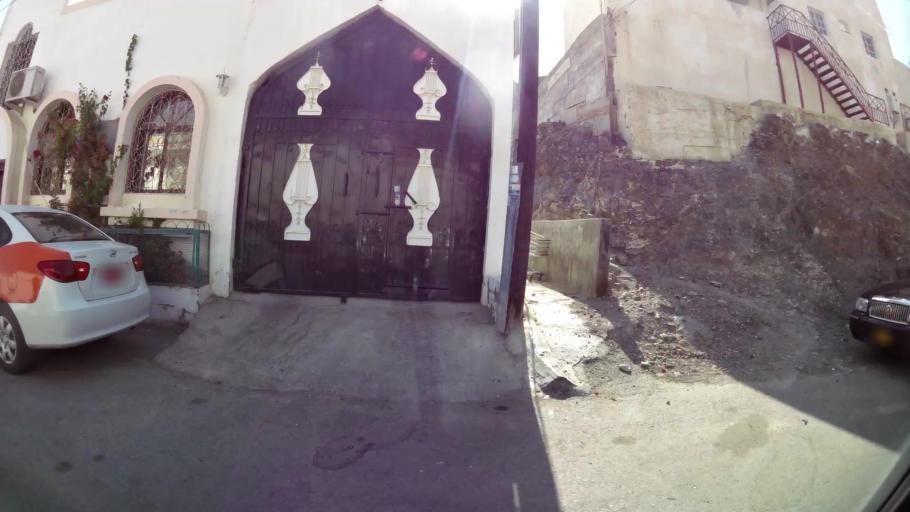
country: OM
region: Muhafazat Masqat
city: Muscat
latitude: 23.6043
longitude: 58.5543
